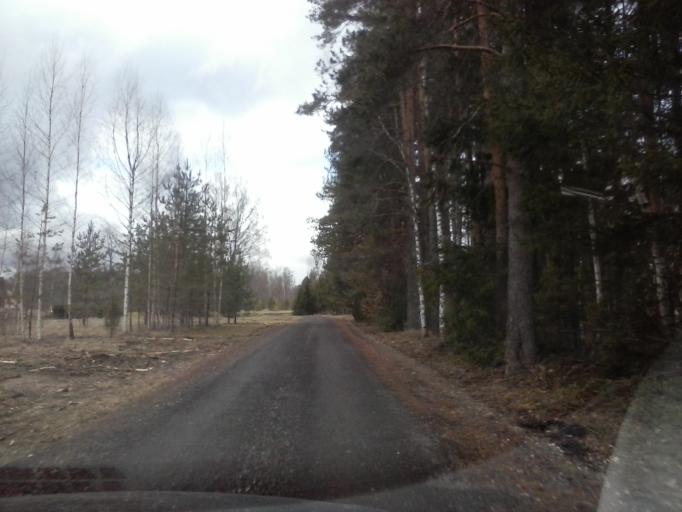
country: EE
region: Jogevamaa
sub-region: Mustvee linn
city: Mustvee
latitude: 59.0256
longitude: 27.0918
